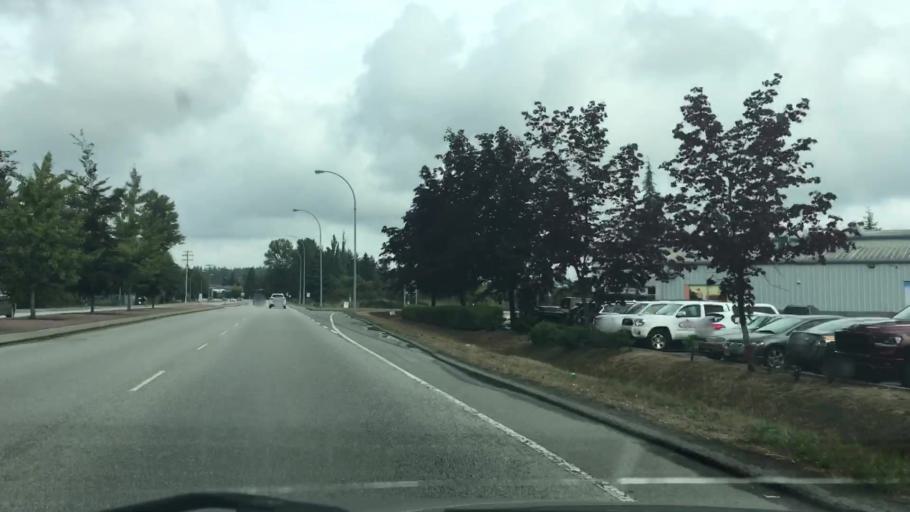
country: CA
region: British Columbia
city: Langley
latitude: 49.1055
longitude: -122.6428
